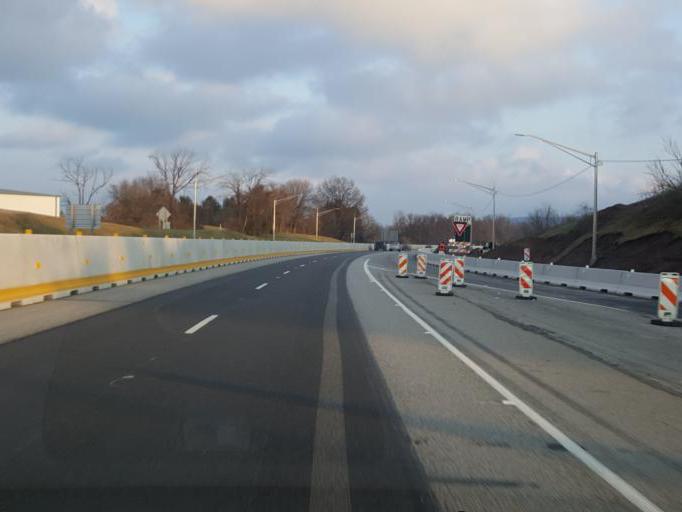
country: US
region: Pennsylvania
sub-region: Cumberland County
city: New Cumberland
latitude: 40.2120
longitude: -76.8730
